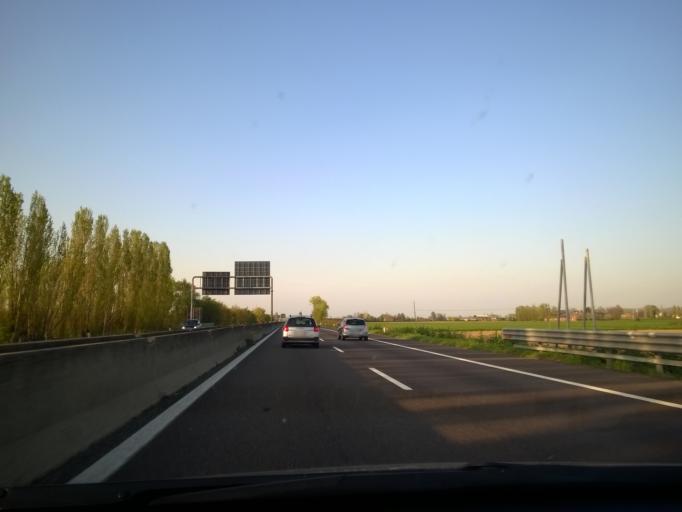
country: IT
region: Emilia-Romagna
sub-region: Provincia di Bologna
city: Progresso
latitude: 44.5416
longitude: 11.3675
